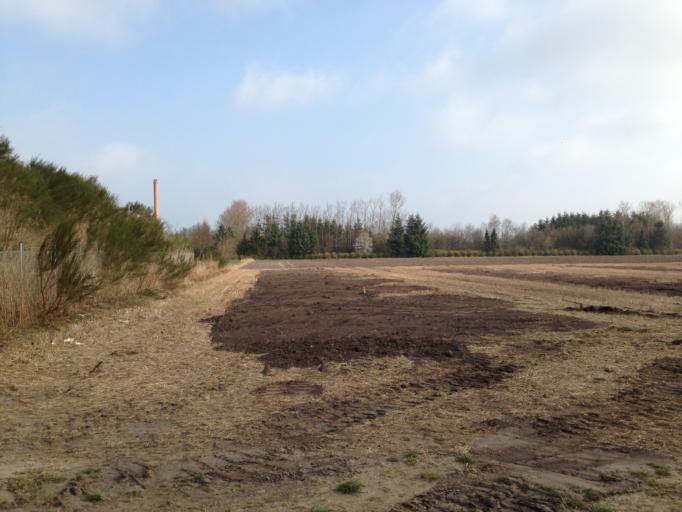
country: DK
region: Central Jutland
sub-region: Herning Kommune
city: Sunds
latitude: 56.1933
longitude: 9.0226
